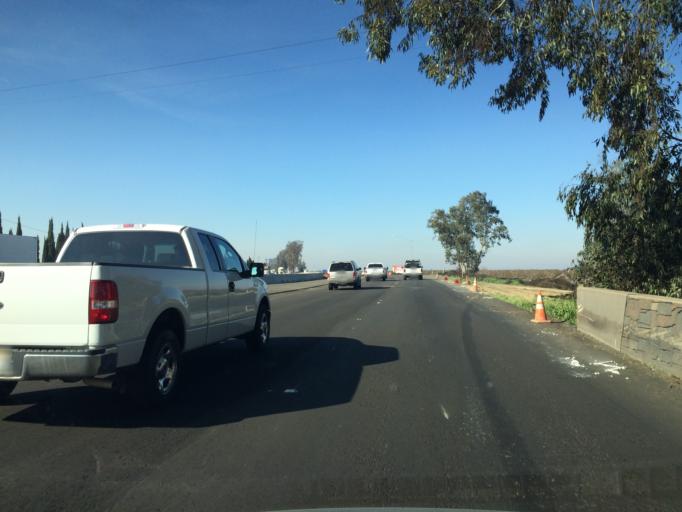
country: US
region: California
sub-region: Tulare County
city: London
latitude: 36.4588
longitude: -119.4927
